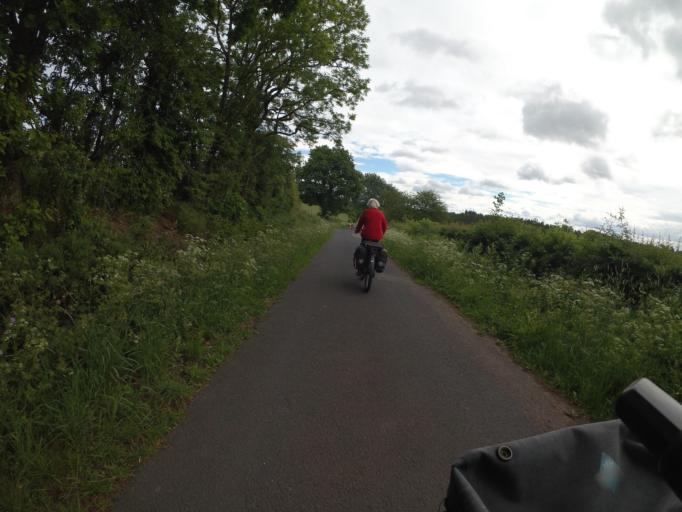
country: DE
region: North Rhine-Westphalia
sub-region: Regierungsbezirk Koln
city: Hellenthal
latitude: 50.4222
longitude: 6.3994
